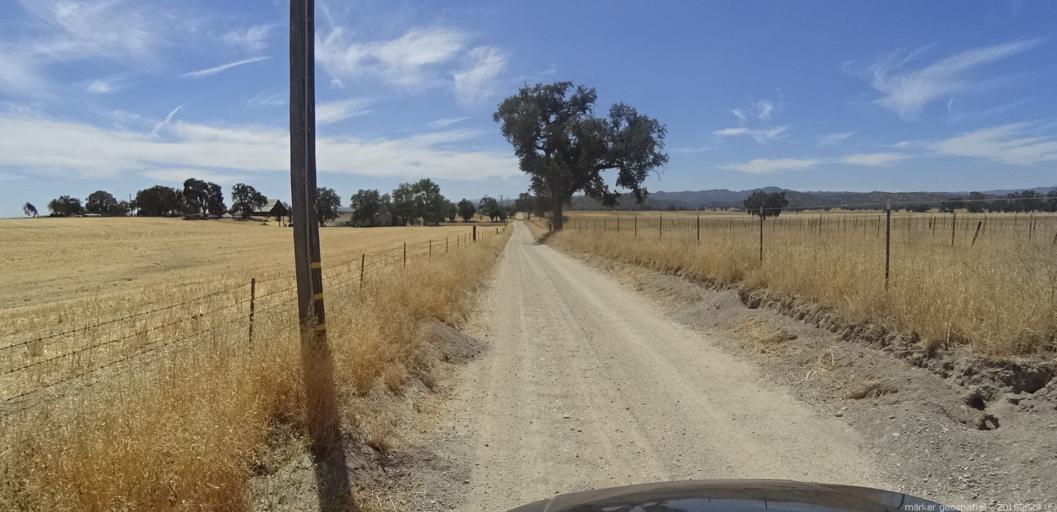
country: US
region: California
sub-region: Monterey County
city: King City
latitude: 35.9427
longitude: -121.0731
